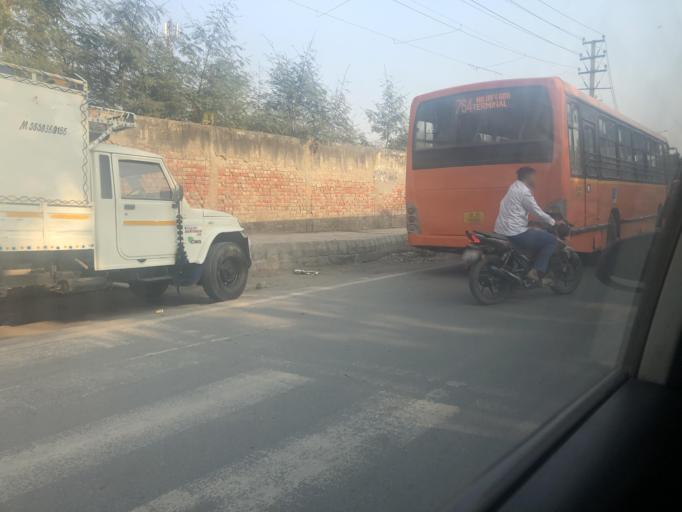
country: IN
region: Haryana
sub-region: Jhajjar
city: Bahadurgarh
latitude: 28.6155
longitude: 76.9764
